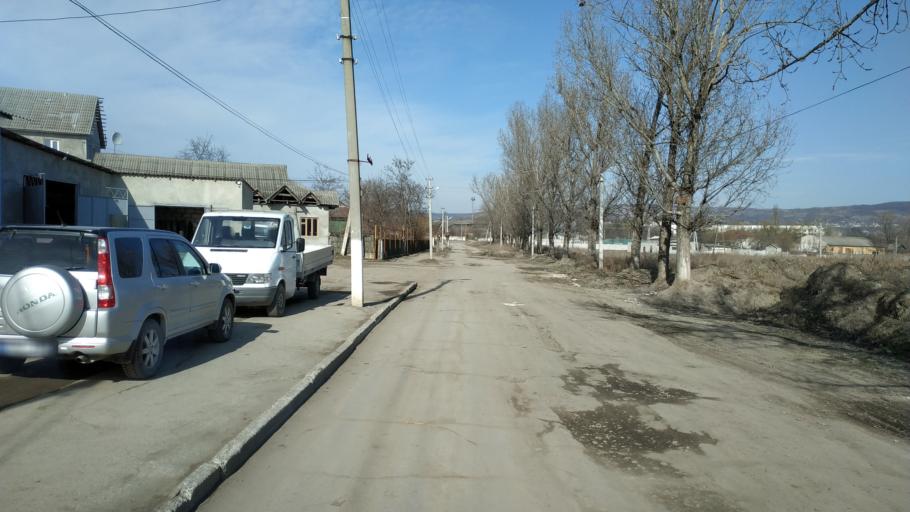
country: MD
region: Nisporeni
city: Nisporeni
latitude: 47.0704
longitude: 28.1749
